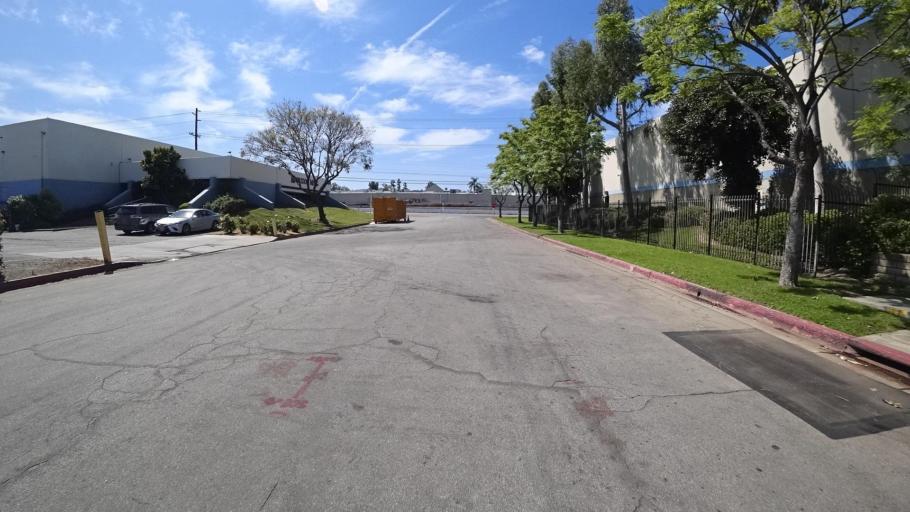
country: US
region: California
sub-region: Los Angeles County
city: South San Jose Hills
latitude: 33.9975
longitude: -117.9100
